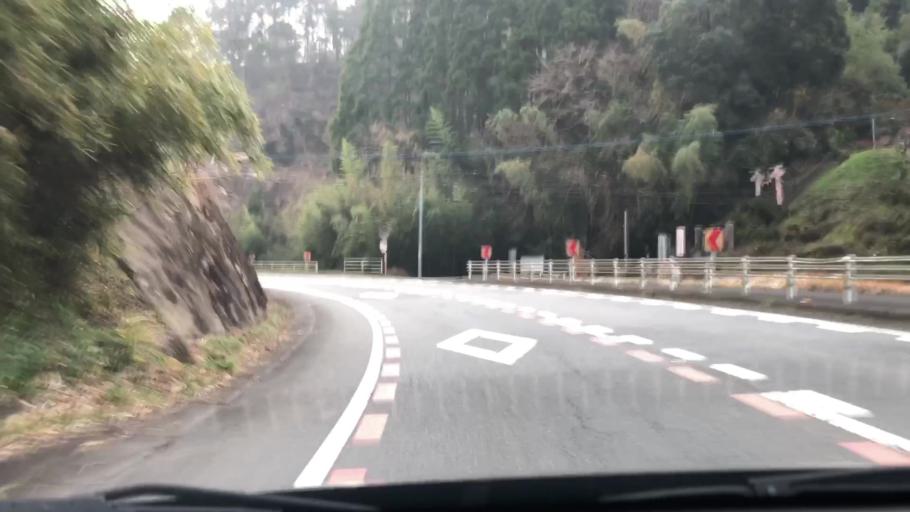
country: JP
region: Oita
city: Takedamachi
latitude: 32.9783
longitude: 131.5471
